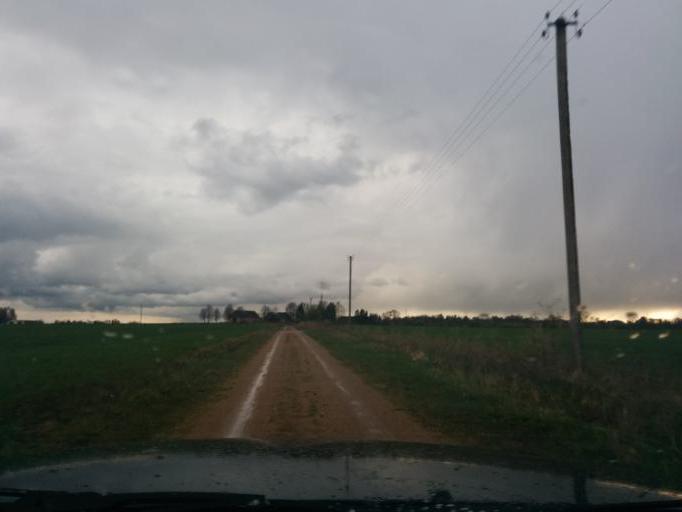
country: LV
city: Tervete
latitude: 56.3691
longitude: 23.5101
